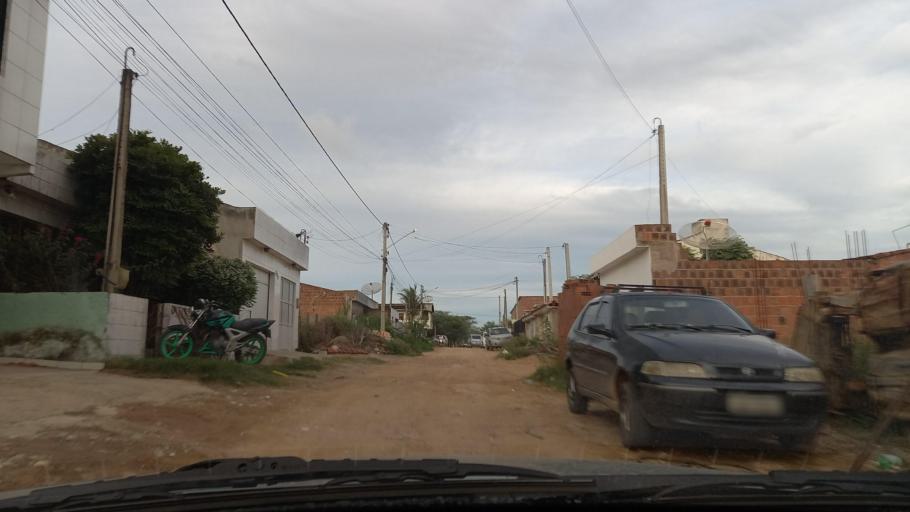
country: BR
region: Pernambuco
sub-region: Gravata
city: Gravata
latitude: -8.1935
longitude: -35.5787
